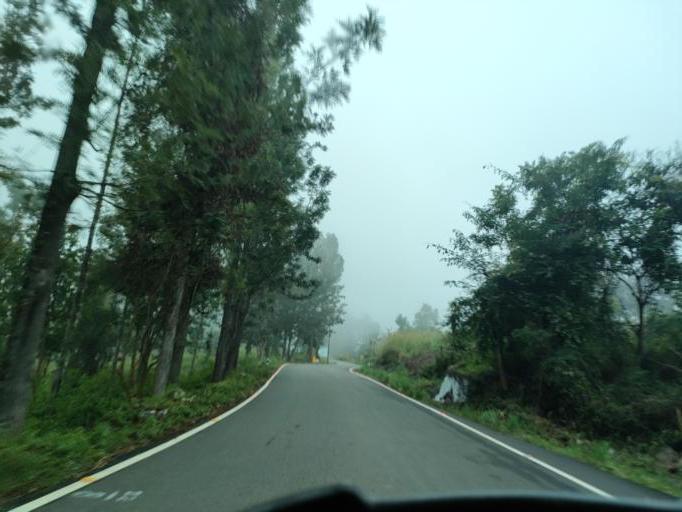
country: IN
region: Tamil Nadu
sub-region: Dindigul
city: Ayakudi
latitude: 10.3570
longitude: 77.5623
